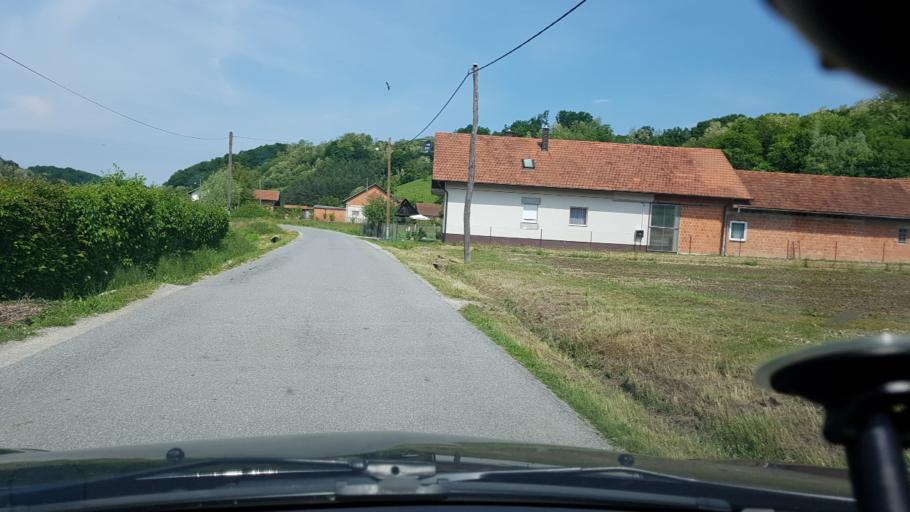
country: HR
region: Krapinsko-Zagorska
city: Selnica
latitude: 46.0276
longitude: 16.0420
